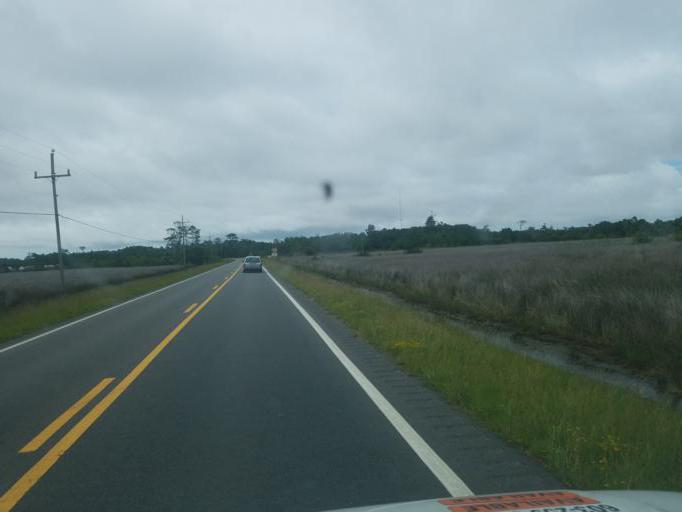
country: US
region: North Carolina
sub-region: Dare County
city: Wanchese
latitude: 35.8577
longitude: -75.6463
